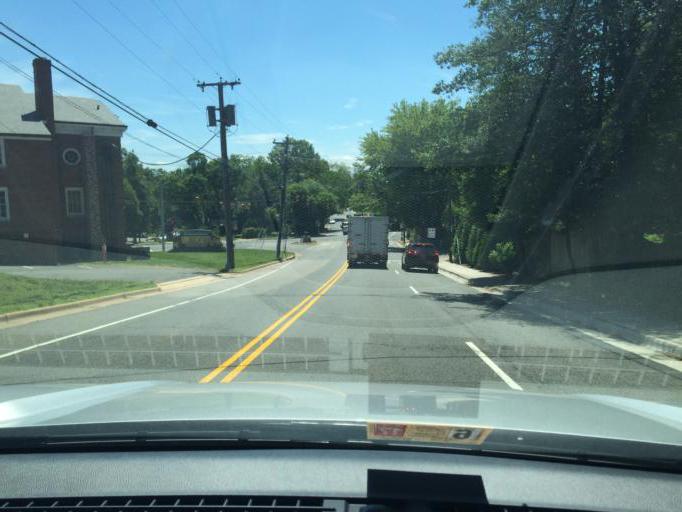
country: US
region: Virginia
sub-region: City of Alexandria
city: Alexandria
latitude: 38.8183
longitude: -77.0671
